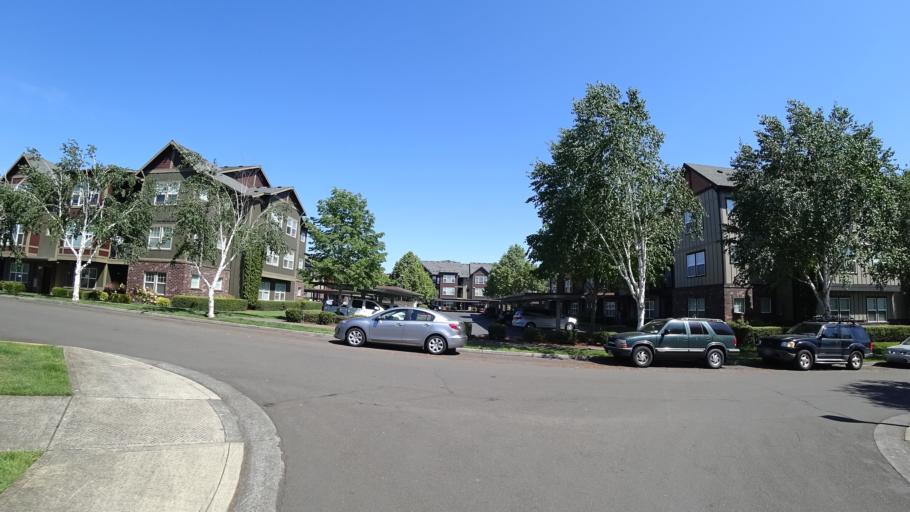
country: US
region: Oregon
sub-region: Washington County
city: Rockcreek
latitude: 45.5287
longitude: -122.9154
